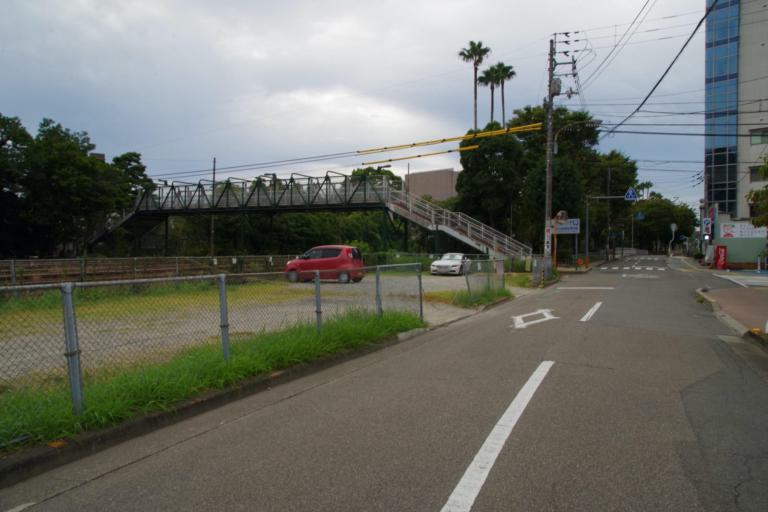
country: JP
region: Tokushima
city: Tokushima-shi
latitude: 34.0724
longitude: 134.5548
